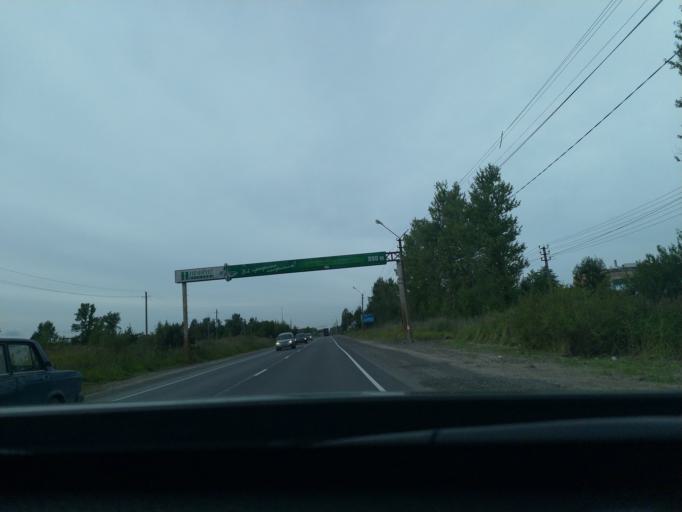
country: RU
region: Leningrad
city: Nikol'skoye
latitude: 59.7209
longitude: 30.7786
